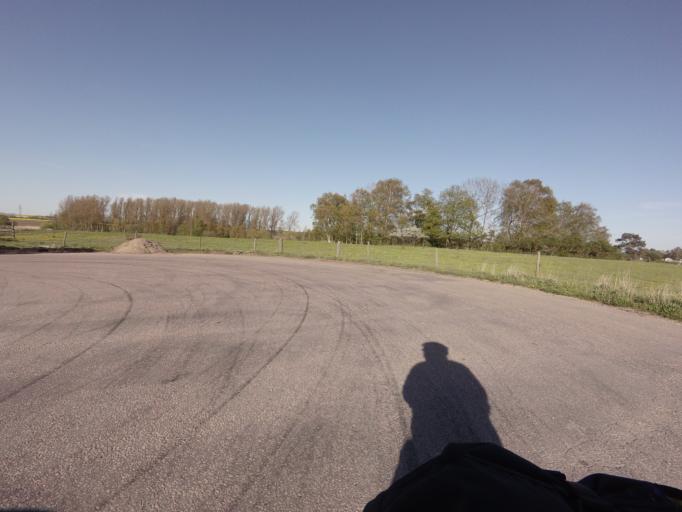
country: SE
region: Skane
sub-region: Landskrona
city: Asmundtorp
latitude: 55.8534
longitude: 12.9253
